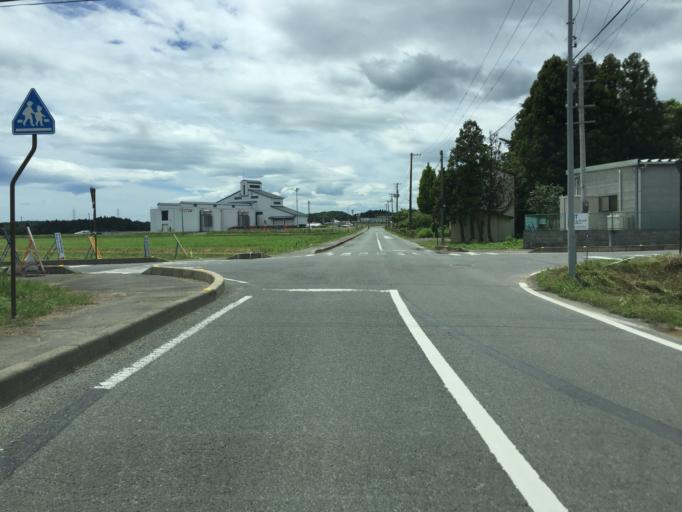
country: JP
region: Fukushima
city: Namie
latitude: 37.6257
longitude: 141.0004
